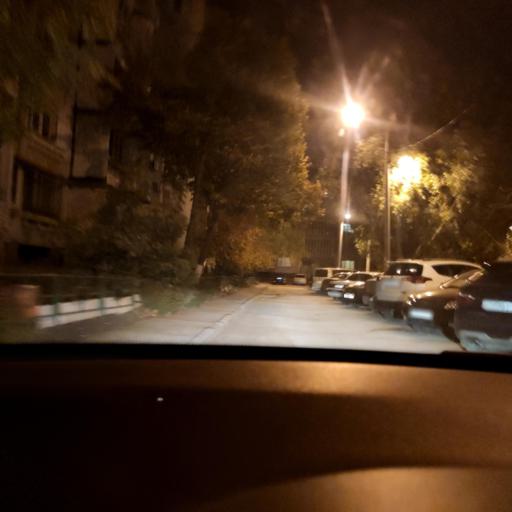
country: RU
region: Samara
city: Samara
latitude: 53.2505
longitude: 50.2108
